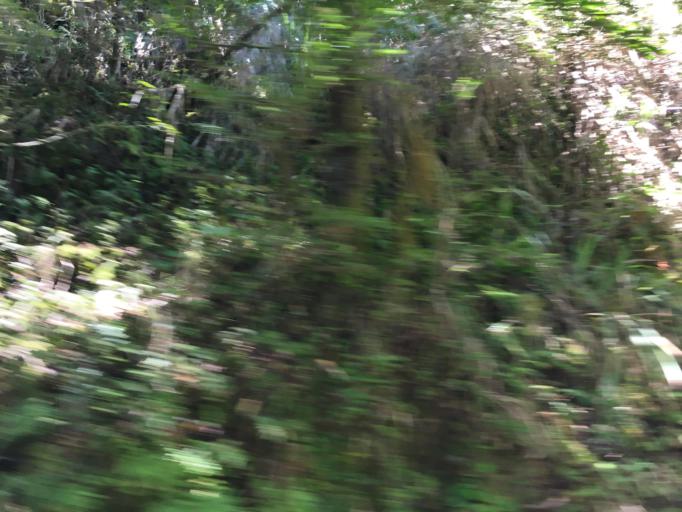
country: TW
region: Taiwan
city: Daxi
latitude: 24.5578
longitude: 121.3978
